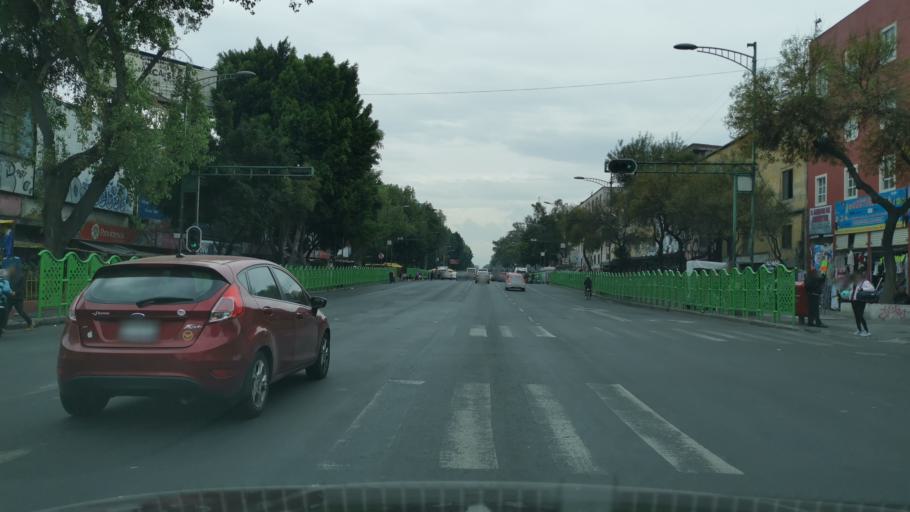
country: MX
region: Mexico City
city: Mexico City
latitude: 19.4329
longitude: -99.1245
